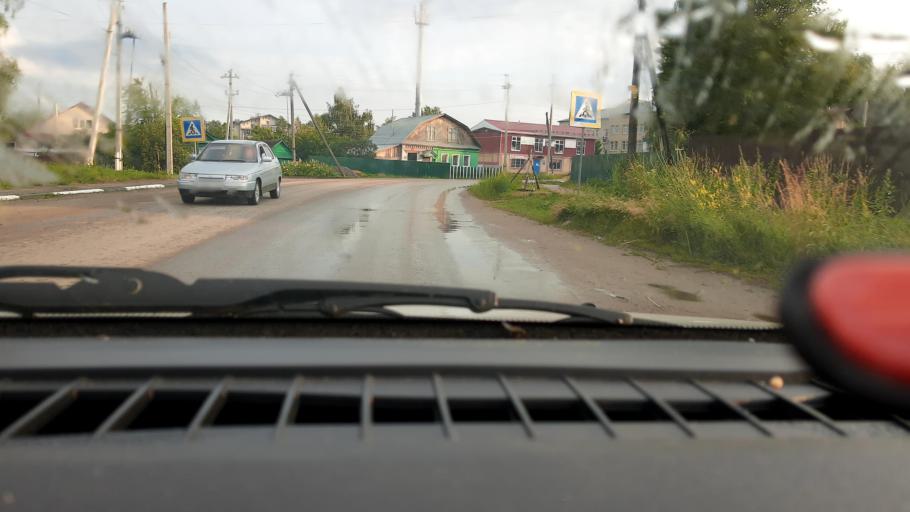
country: RU
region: Nizjnij Novgorod
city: Lukoyanov
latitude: 55.0382
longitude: 44.4951
